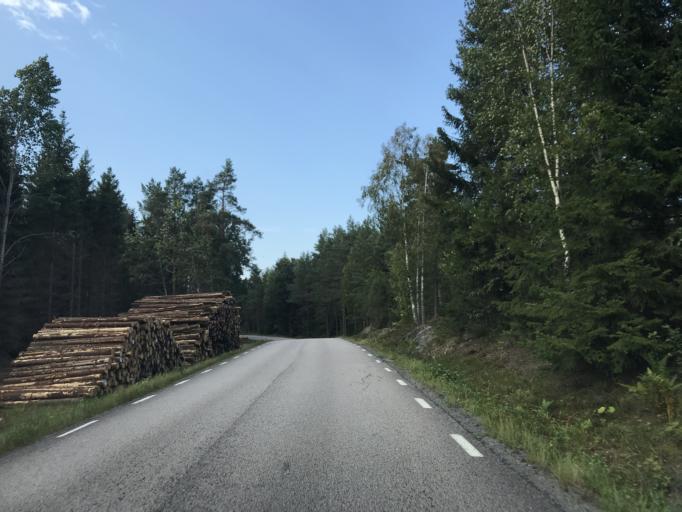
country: SE
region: Stockholm
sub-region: Norrtalje Kommun
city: Bjorko
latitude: 59.8846
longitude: 18.9800
